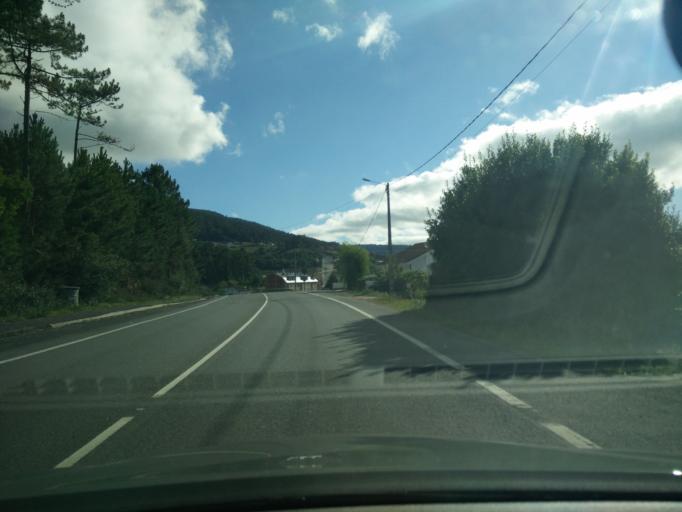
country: ES
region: Galicia
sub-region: Provincia da Coruna
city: Laxe
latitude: 43.2210
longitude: -8.9258
